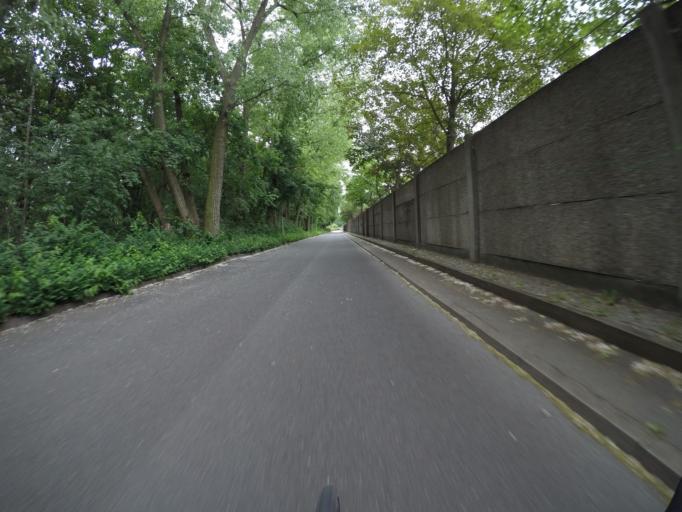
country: DE
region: Berlin
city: Reinickendorf
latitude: 52.5528
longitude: 13.3240
